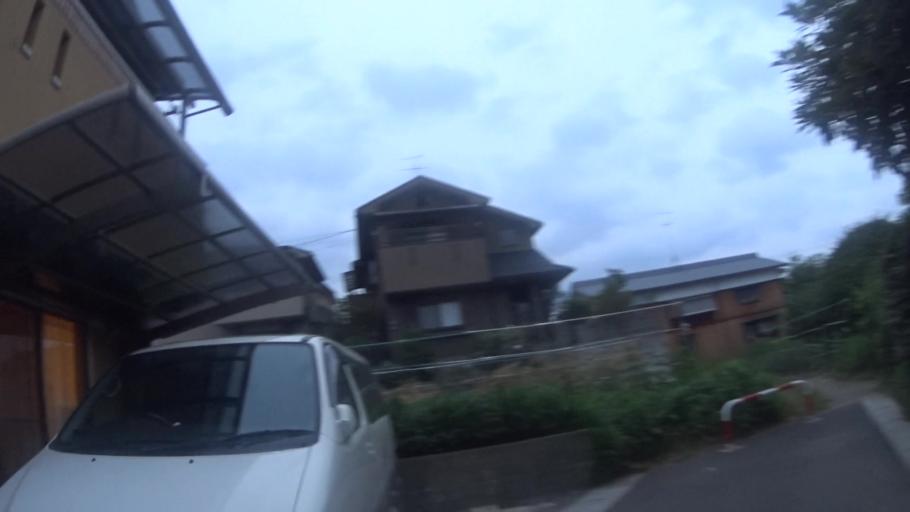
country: JP
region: Kyoto
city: Muko
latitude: 34.9443
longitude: 135.7070
